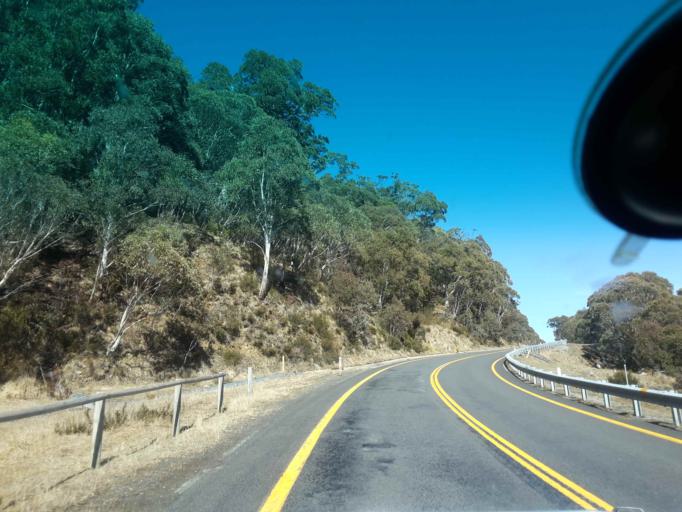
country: AU
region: New South Wales
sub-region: Snowy River
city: Jindabyne
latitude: -36.4905
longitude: 148.3340
